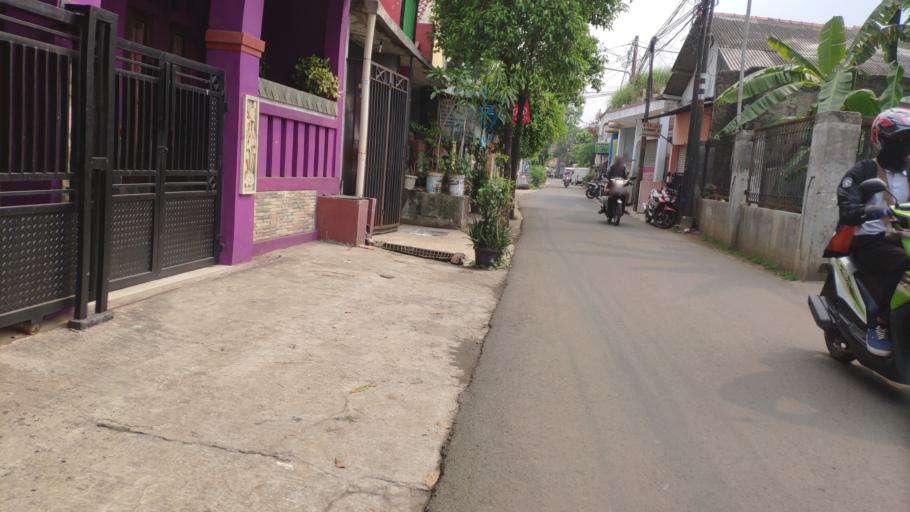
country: ID
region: West Java
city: Depok
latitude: -6.3420
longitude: 106.8159
